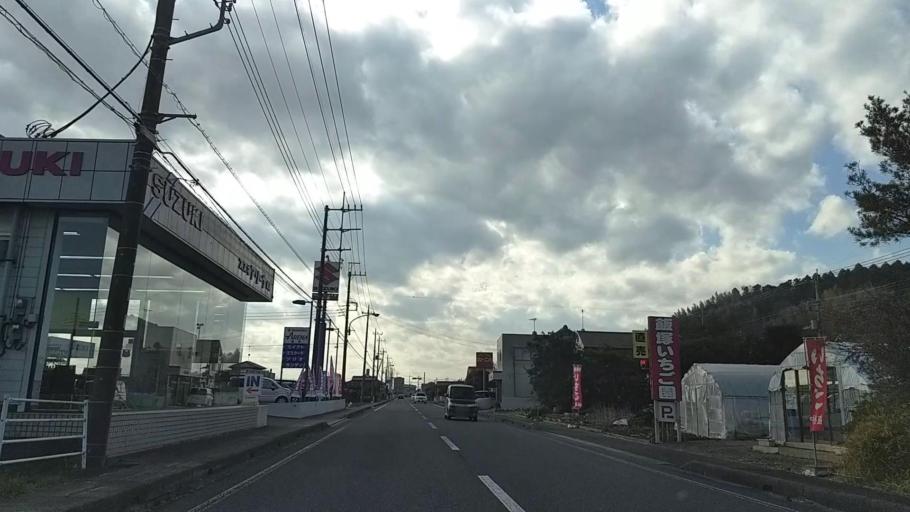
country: JP
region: Chiba
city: Naruto
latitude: 35.6159
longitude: 140.4323
